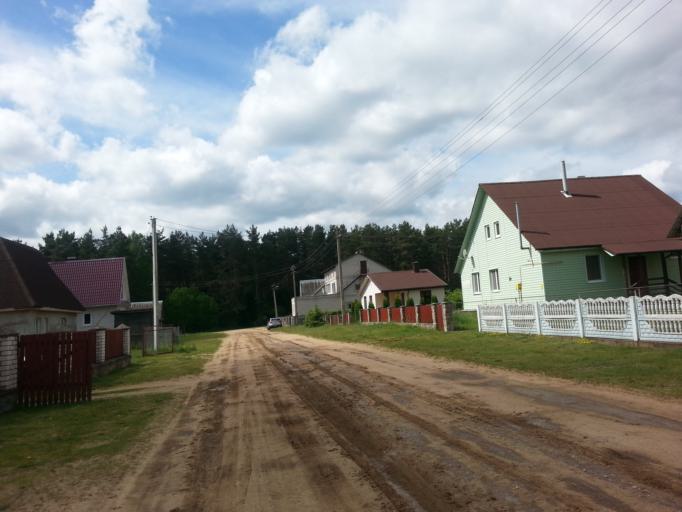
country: BY
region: Minsk
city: Narach
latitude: 54.9241
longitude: 26.6857
